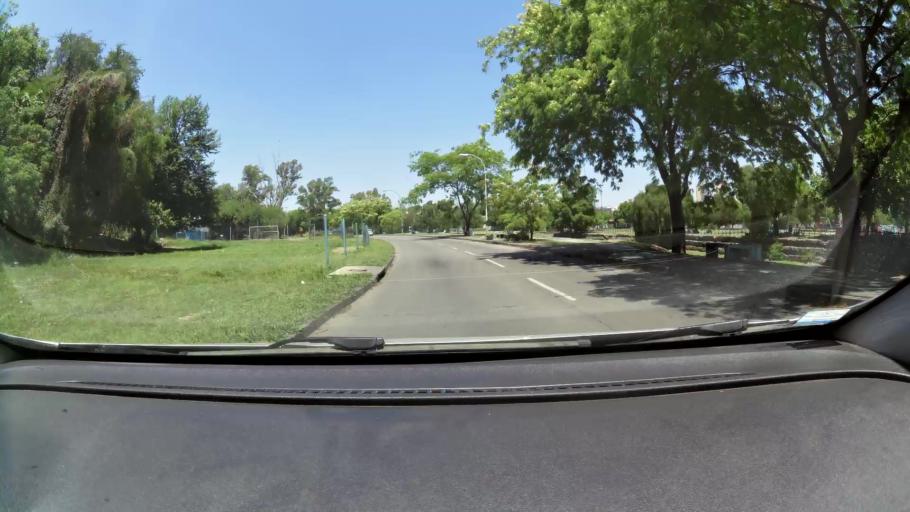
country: AR
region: Cordoba
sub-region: Departamento de Capital
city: Cordoba
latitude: -31.4018
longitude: -64.2037
